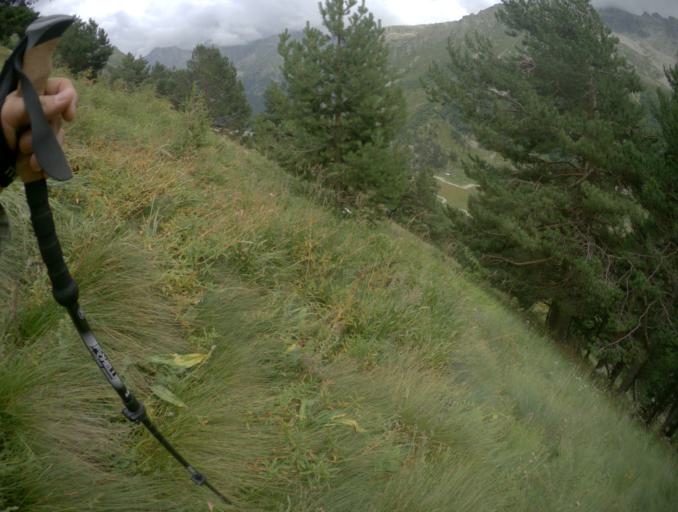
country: RU
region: Karachayevo-Cherkesiya
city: Uchkulan
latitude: 43.2679
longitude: 42.1386
